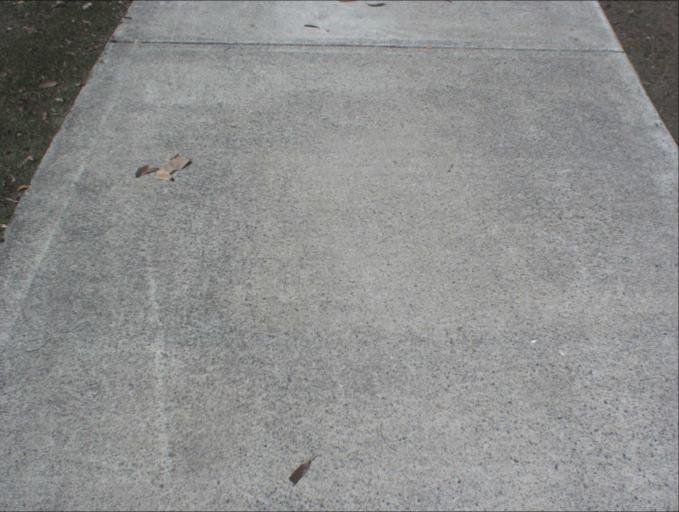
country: AU
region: Queensland
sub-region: Logan
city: Waterford West
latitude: -27.6797
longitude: 153.0930
